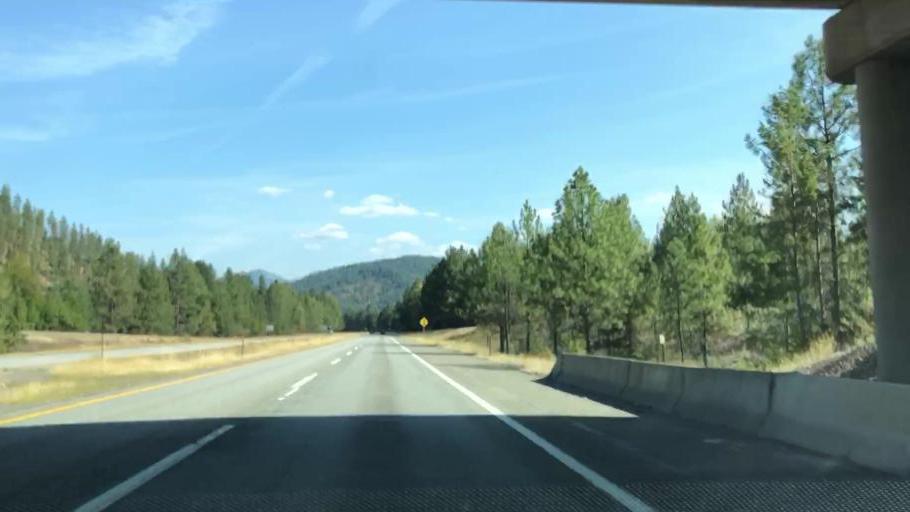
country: US
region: Idaho
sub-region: Shoshone County
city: Pinehurst
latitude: 47.5497
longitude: -116.3527
